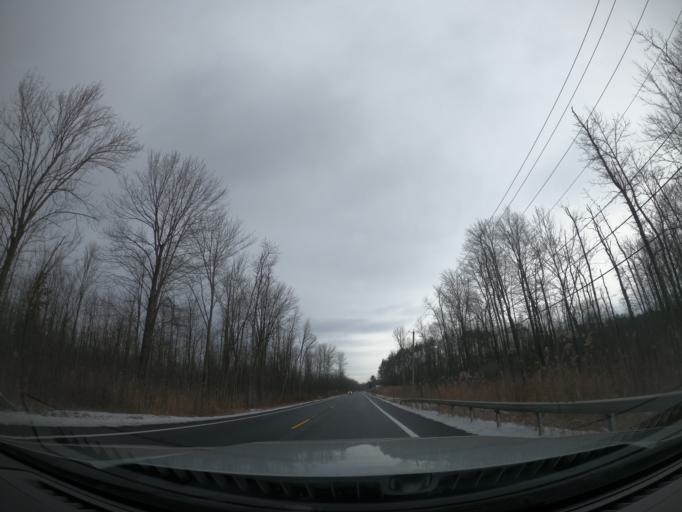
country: US
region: New York
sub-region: Madison County
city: Bridgeport
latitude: 43.1374
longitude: -75.9836
